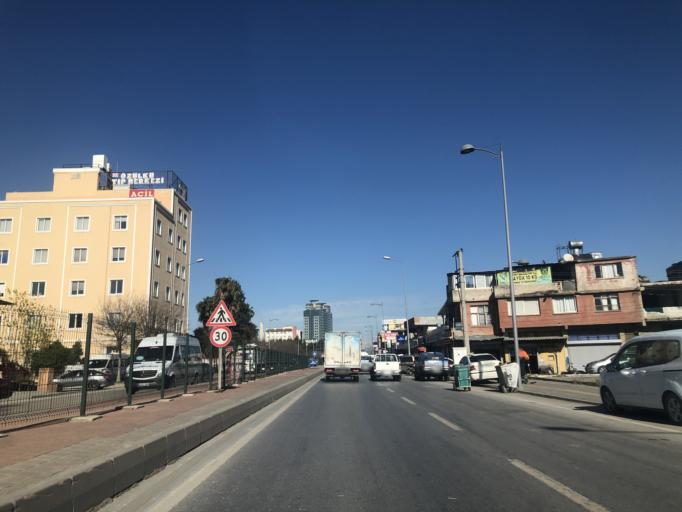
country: TR
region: Adana
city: Yuregir
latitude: 36.9812
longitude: 35.3384
